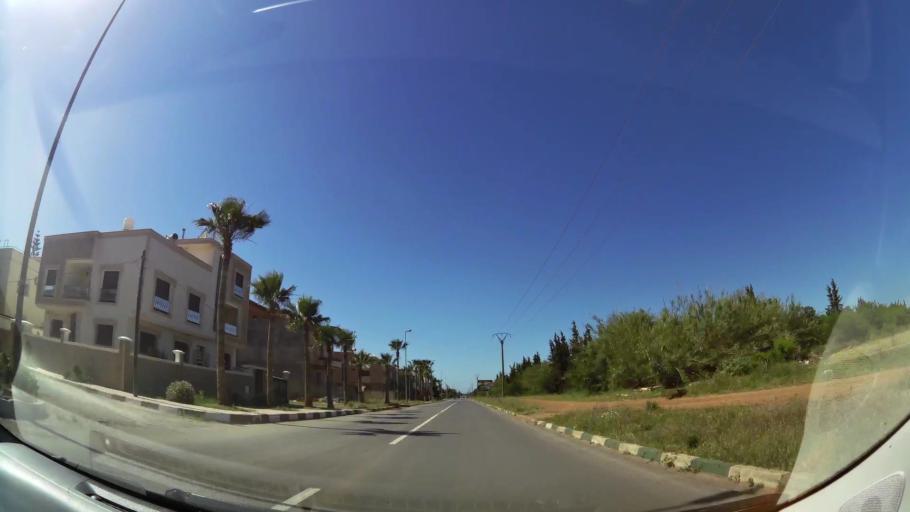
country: MA
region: Oriental
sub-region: Berkane-Taourirt
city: Berkane
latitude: 34.9413
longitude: -2.3252
